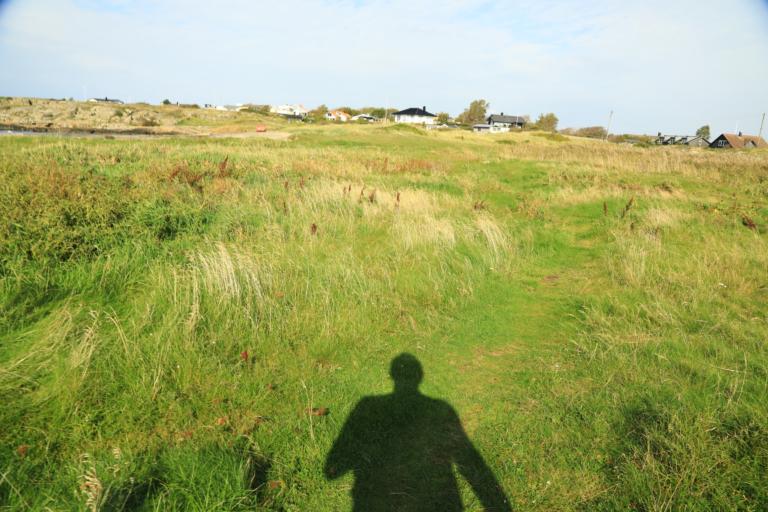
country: SE
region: Halland
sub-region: Varbergs Kommun
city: Varberg
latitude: 57.1138
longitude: 12.2130
